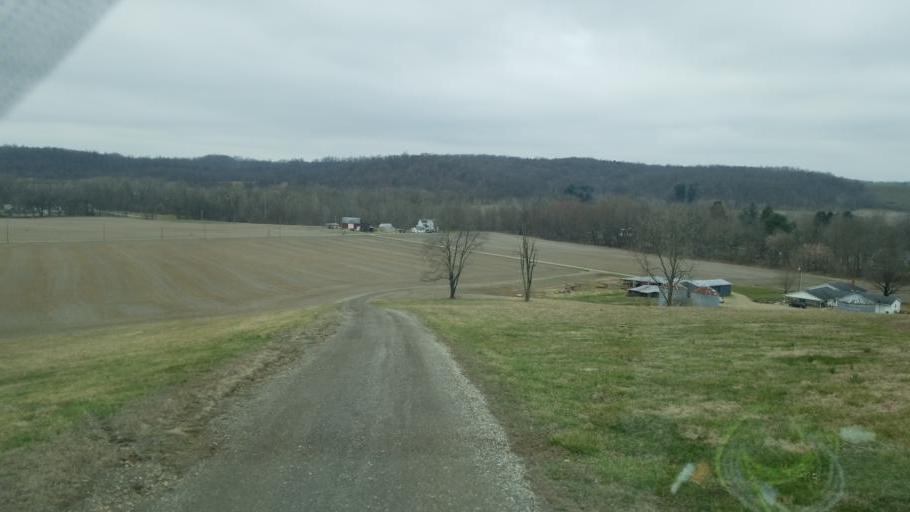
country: US
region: Ohio
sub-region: Licking County
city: Utica
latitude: 40.1589
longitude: -82.4487
